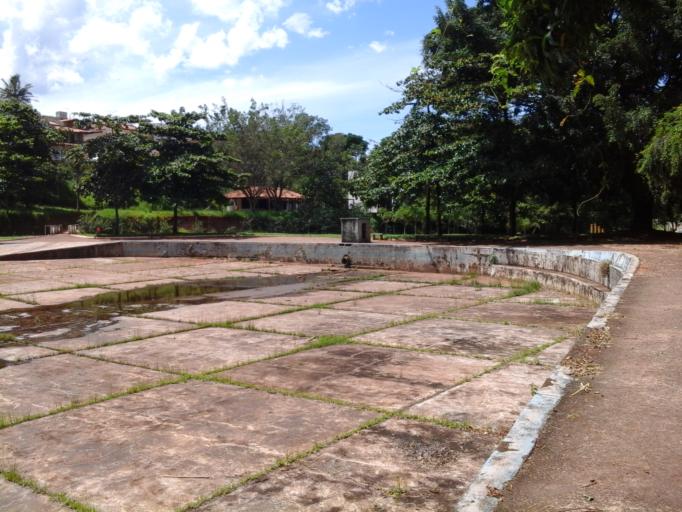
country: BR
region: Minas Gerais
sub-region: Patos De Minas
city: Patos de Minas
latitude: -18.5845
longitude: -46.5055
